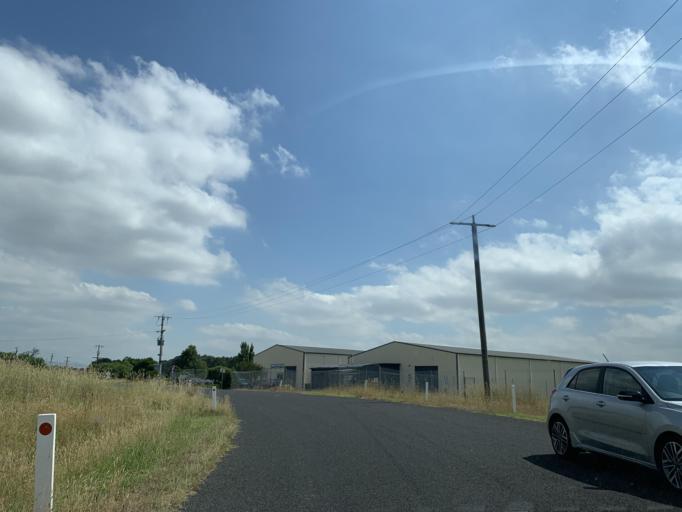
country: AU
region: Victoria
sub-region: Latrobe
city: Traralgon
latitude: -38.2138
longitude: 146.4698
